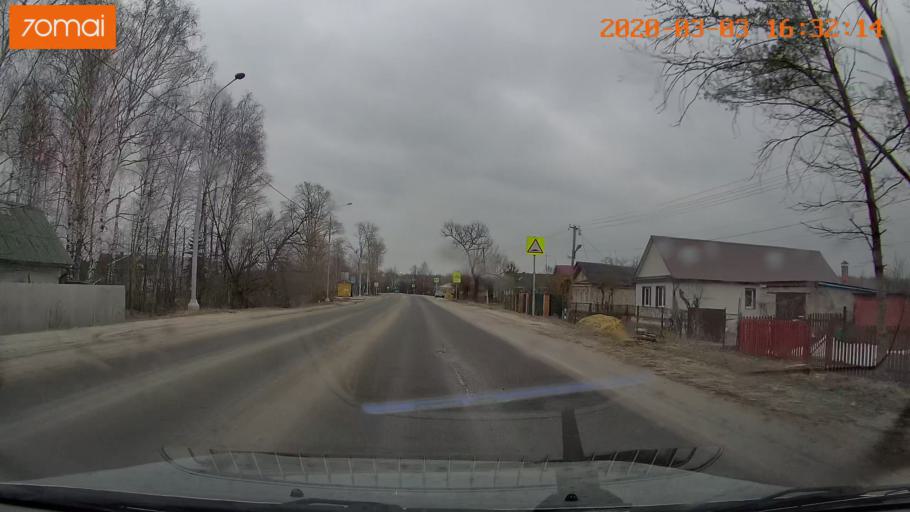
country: RU
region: Moskovskaya
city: Konobeyevo
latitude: 55.4214
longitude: 38.7317
